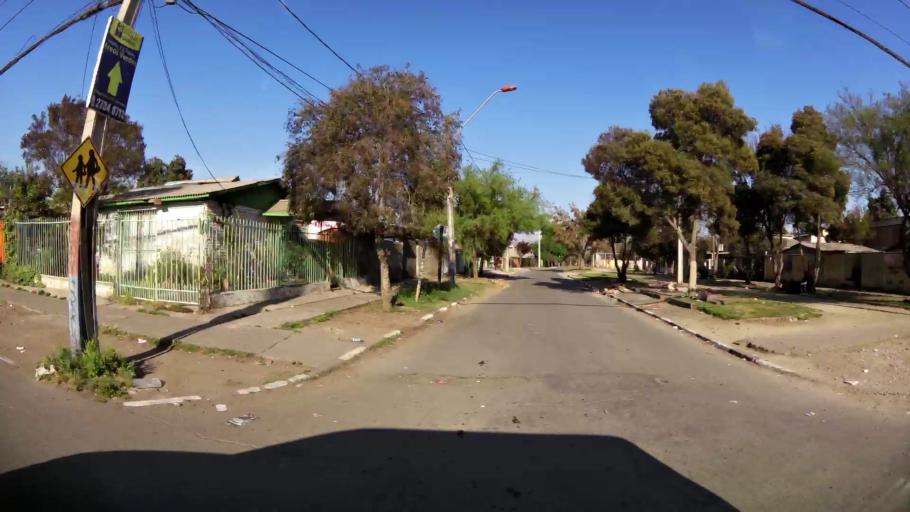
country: CL
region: Santiago Metropolitan
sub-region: Provincia de Santiago
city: Santiago
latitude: -33.3792
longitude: -70.6610
